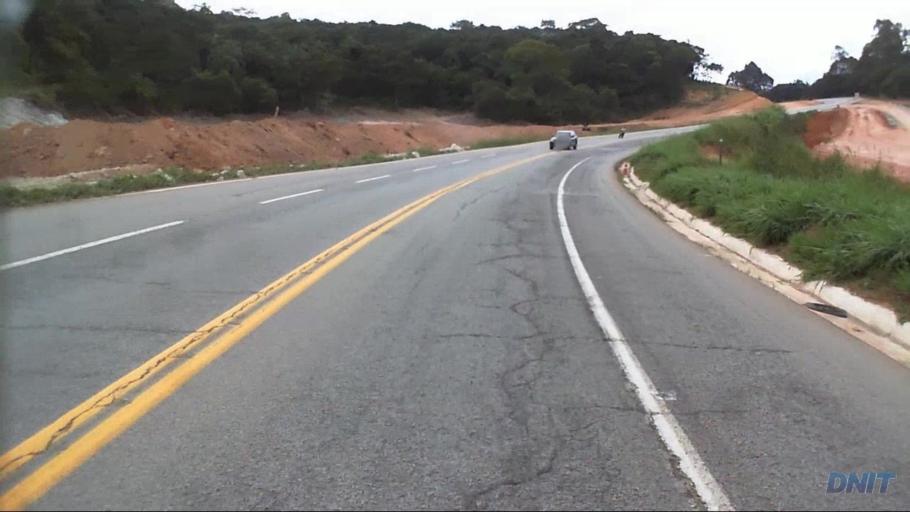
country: BR
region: Minas Gerais
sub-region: Caete
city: Caete
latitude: -19.7469
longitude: -43.5476
